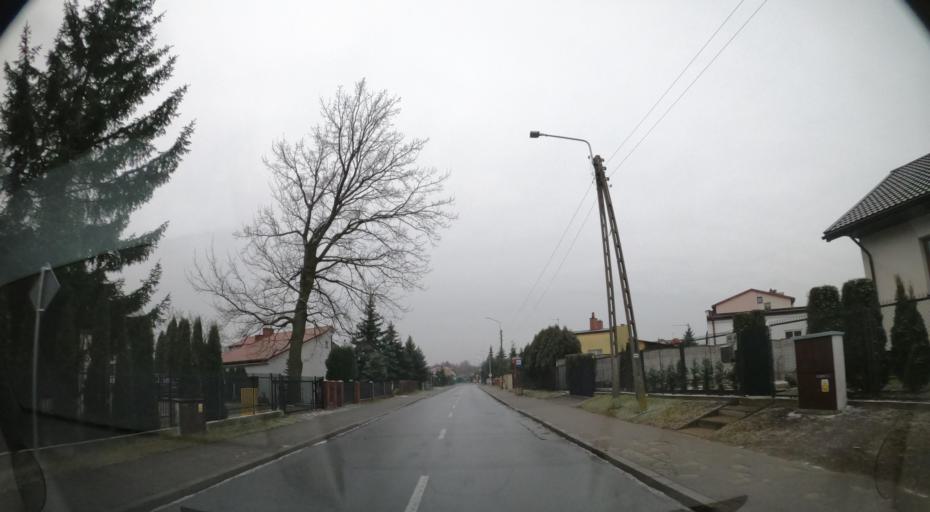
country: PL
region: Masovian Voivodeship
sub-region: Powiat radomski
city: Trablice
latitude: 51.3794
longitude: 21.1000
